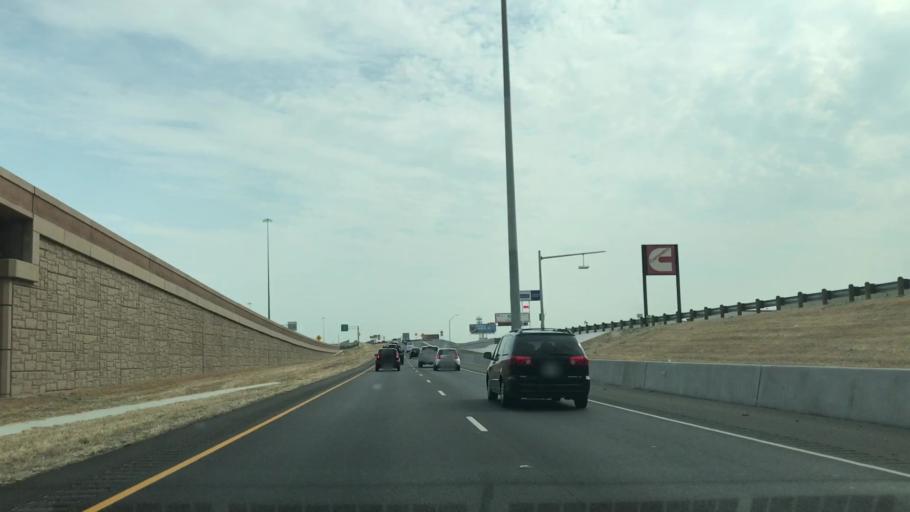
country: US
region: Texas
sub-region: Tarrant County
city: Haltom City
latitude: 32.8019
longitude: -97.3192
